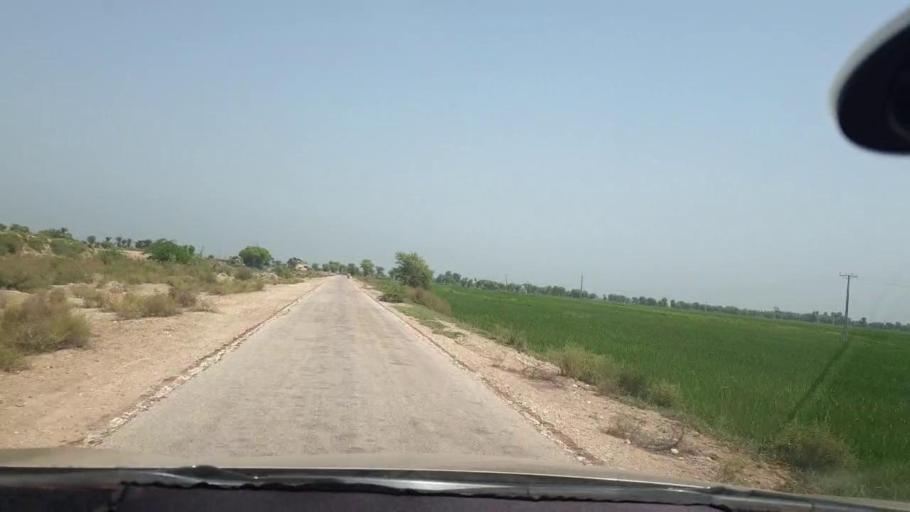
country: PK
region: Sindh
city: Kambar
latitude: 27.6850
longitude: 67.9491
